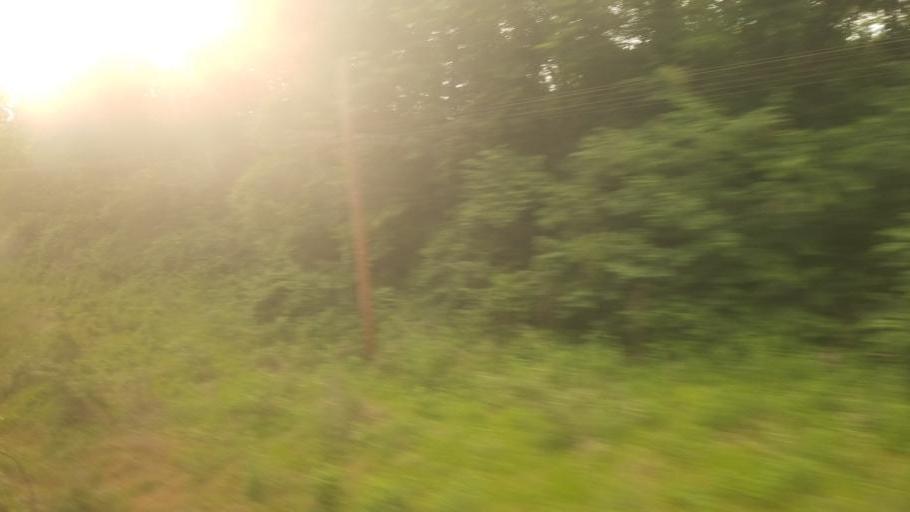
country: US
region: Kansas
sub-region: Osage County
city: Carbondale
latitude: 38.8690
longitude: -95.6935
